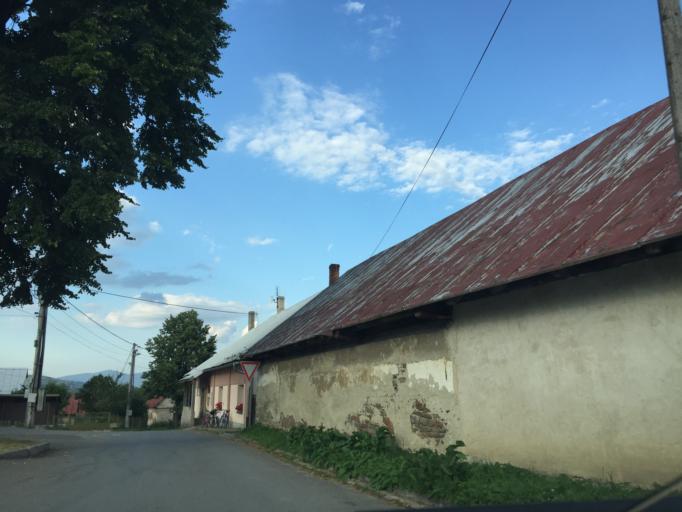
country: PL
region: Silesian Voivodeship
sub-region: Powiat zywiecki
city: Korbielow
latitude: 49.4599
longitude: 19.3240
